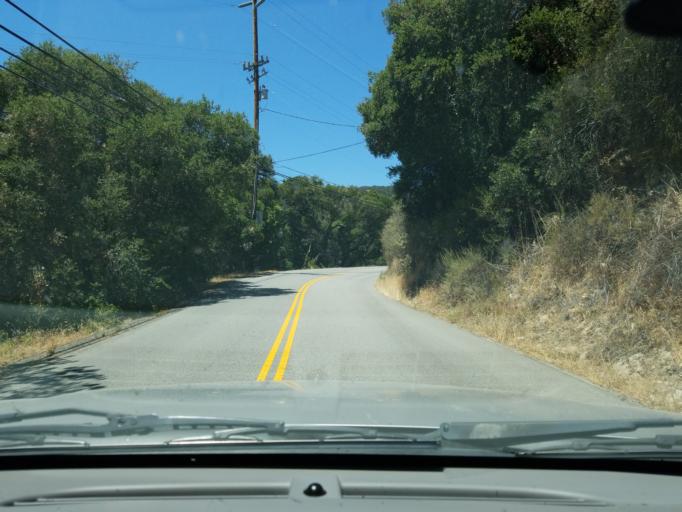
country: US
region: California
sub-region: Monterey County
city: Carmel Valley Village
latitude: 36.4614
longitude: -121.7094
